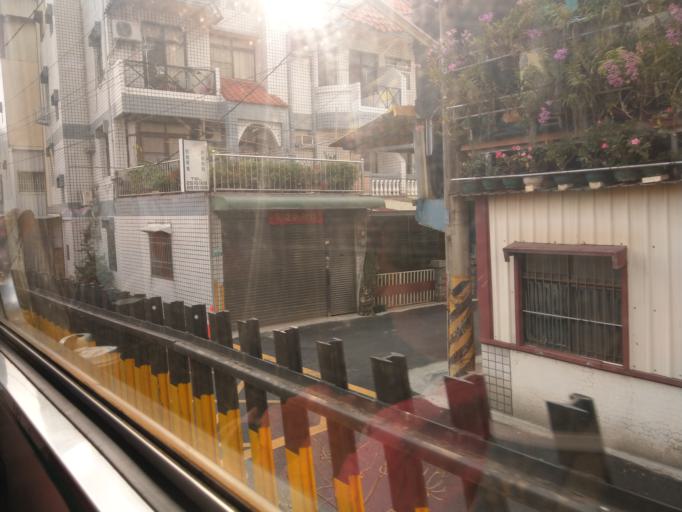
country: TW
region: Taiwan
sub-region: Chiayi
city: Jiayi Shi
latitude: 23.5231
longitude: 120.5499
